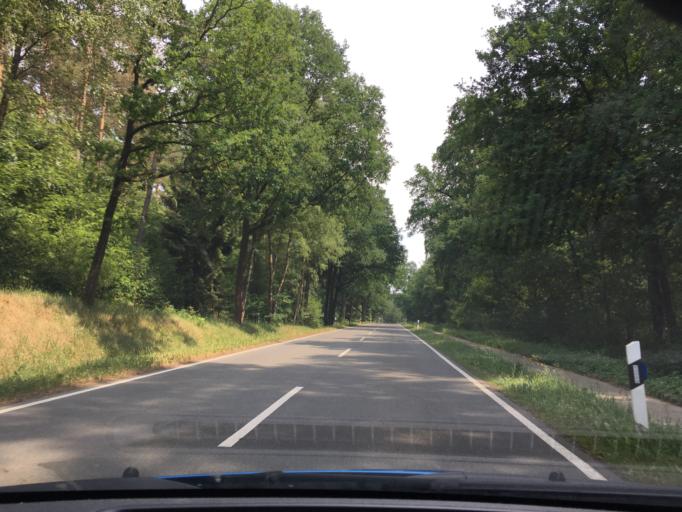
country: DE
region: Lower Saxony
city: Jesteburg
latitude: 53.2703
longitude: 9.9514
